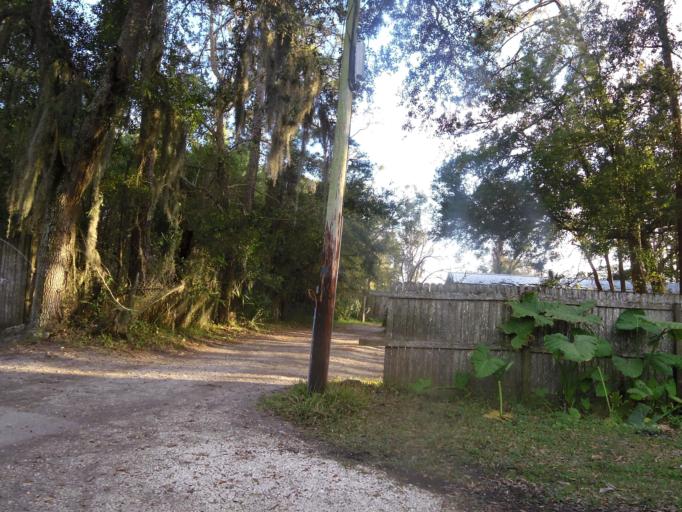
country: US
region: Florida
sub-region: Duval County
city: Jacksonville
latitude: 30.2873
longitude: -81.6422
